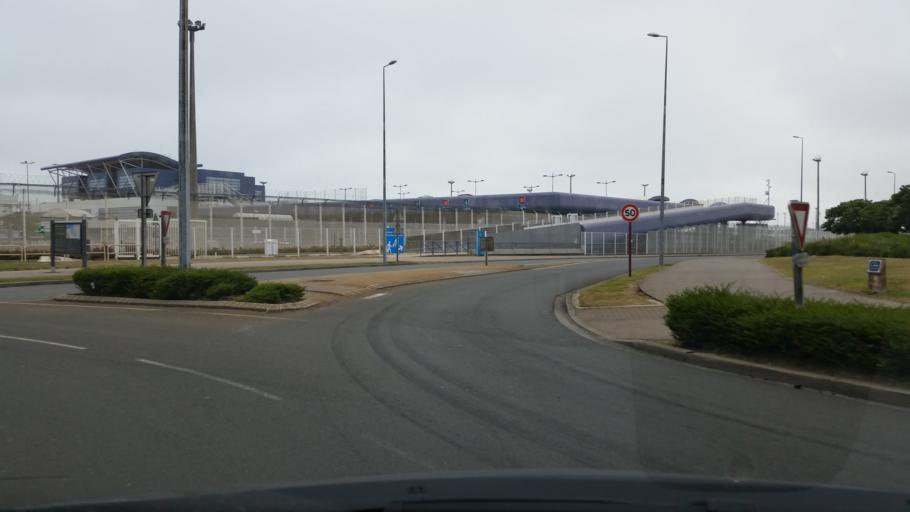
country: FR
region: Nord-Pas-de-Calais
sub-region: Departement du Pas-de-Calais
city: Calais
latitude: 50.9645
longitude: 1.8615
